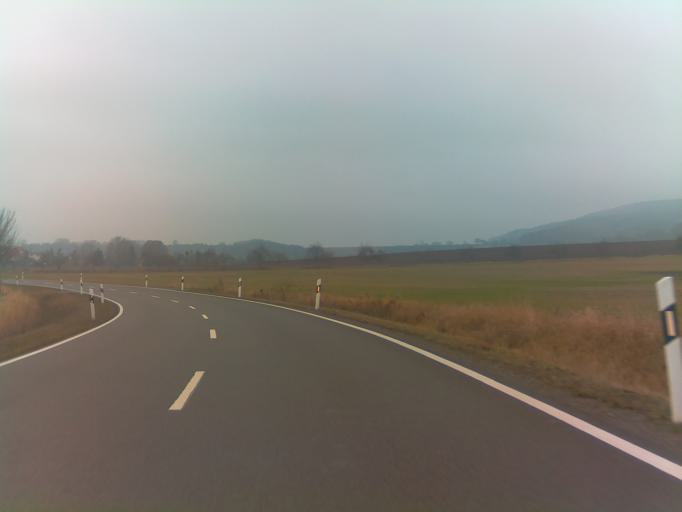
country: DE
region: Thuringia
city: Romhild
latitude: 50.4315
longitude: 10.5085
